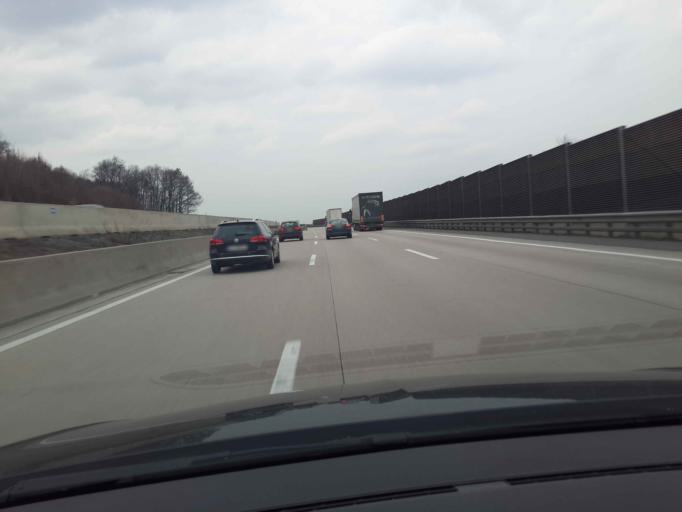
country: AT
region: Lower Austria
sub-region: Politischer Bezirk Sankt Polten
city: Neulengbach
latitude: 48.1724
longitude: 15.8742
